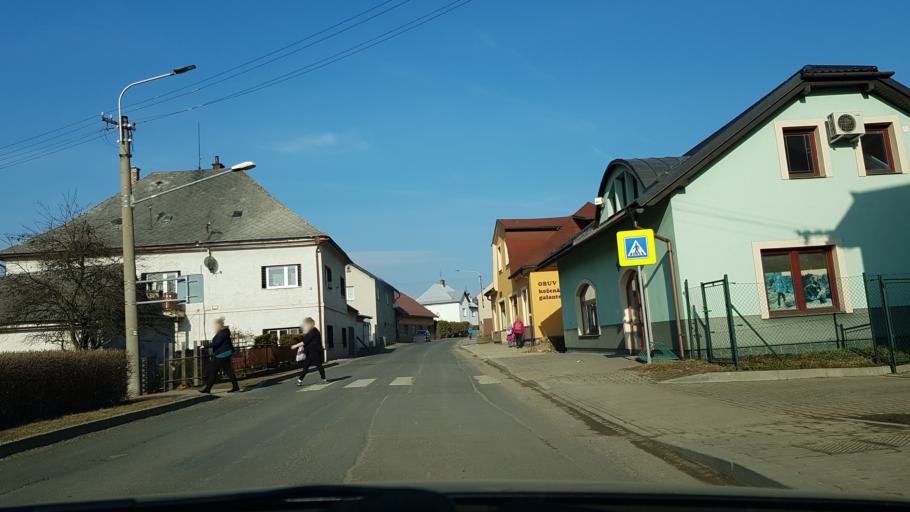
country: CZ
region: Olomoucky
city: Ruda nad Moravou
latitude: 49.9790
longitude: 16.8754
